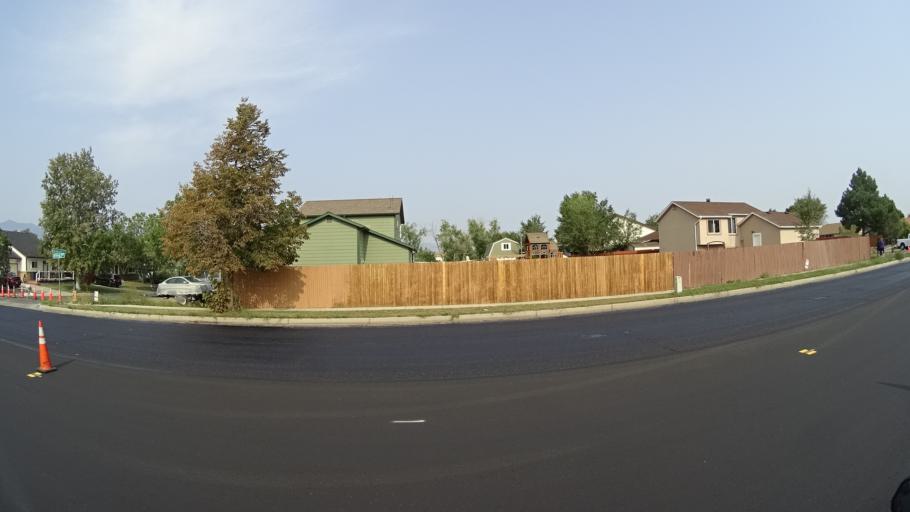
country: US
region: Colorado
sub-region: El Paso County
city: Stratmoor
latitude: 38.8066
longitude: -104.7432
